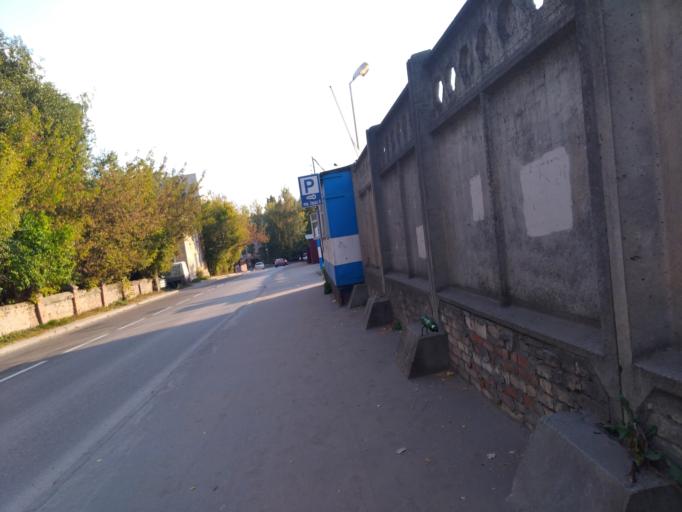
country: RU
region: Kaluga
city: Kaluga
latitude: 54.5231
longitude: 36.2528
